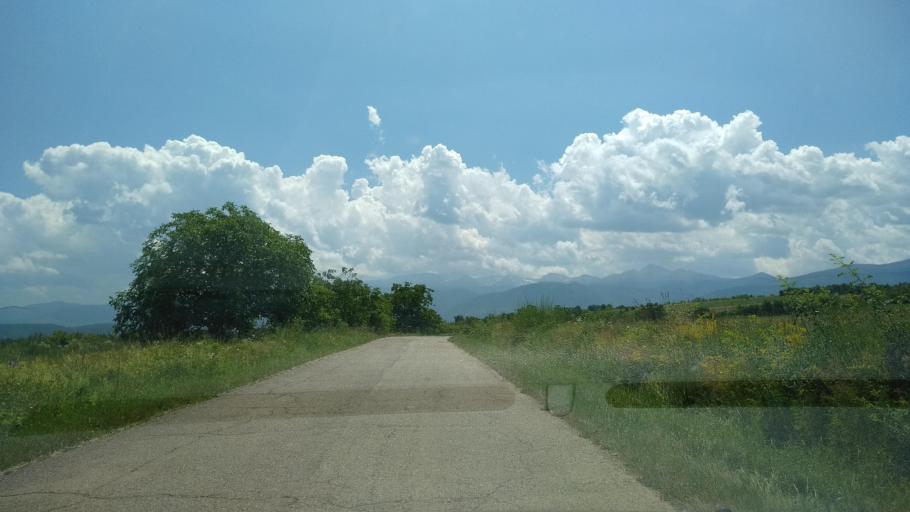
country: RO
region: Hunedoara
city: Densus
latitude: 45.5638
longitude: 22.8151
